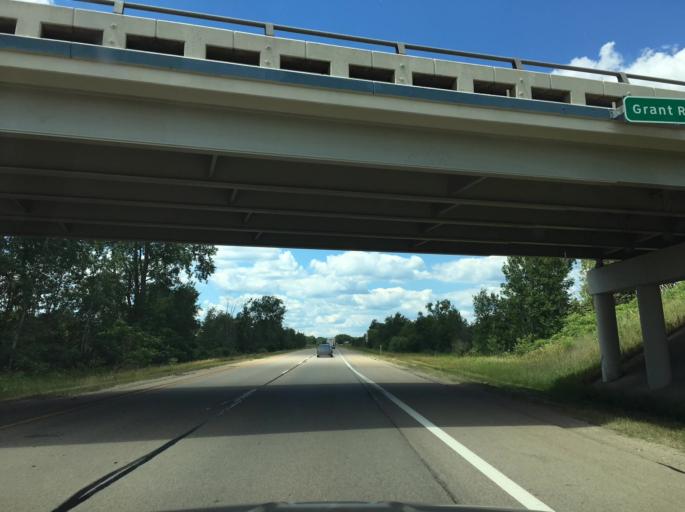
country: US
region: Michigan
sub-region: Clare County
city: Clare
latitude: 43.8815
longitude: -84.7879
